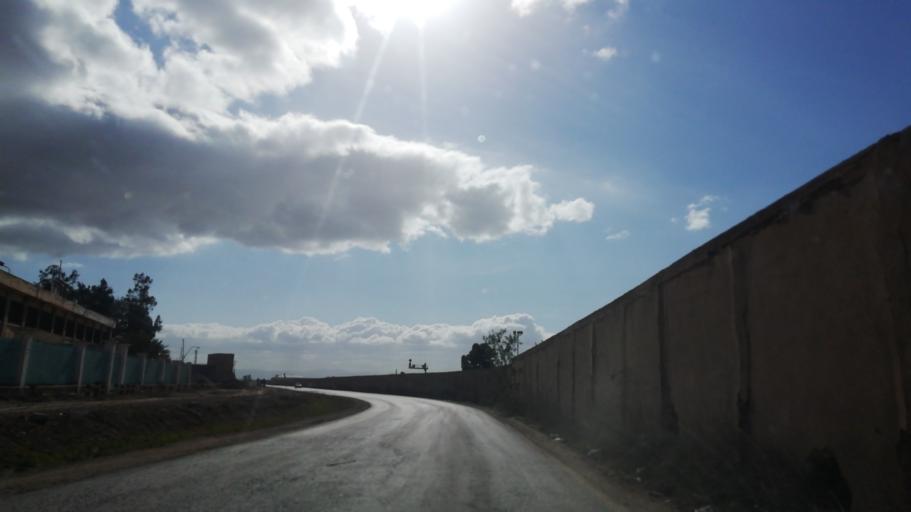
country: DZ
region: Oran
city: Es Senia
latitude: 35.6486
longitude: -0.6060
